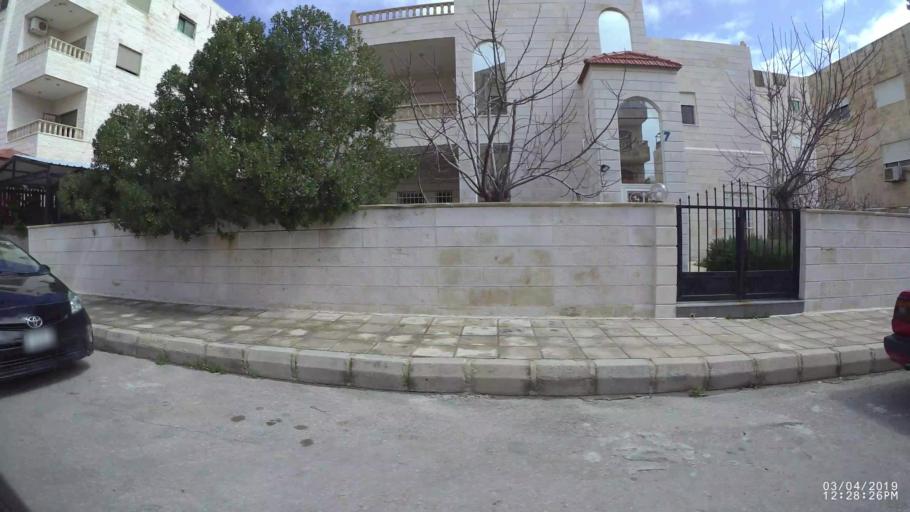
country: JO
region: Amman
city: Wadi as Sir
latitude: 31.9613
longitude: 35.8376
